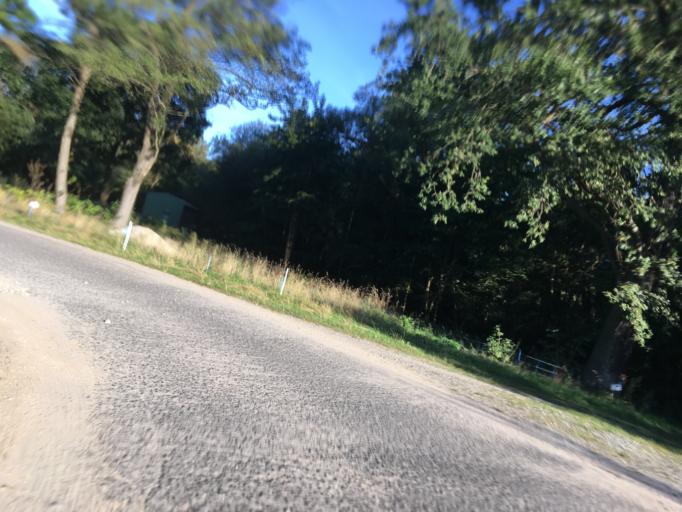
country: DE
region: Saxony
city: Bad Muskau
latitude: 51.5653
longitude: 14.7126
